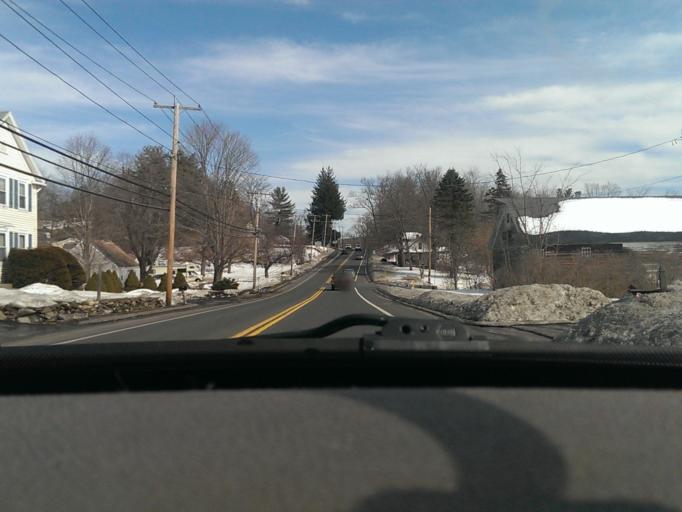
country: US
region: Massachusetts
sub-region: Hampden County
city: Three Rivers
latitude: 42.1525
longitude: -72.3908
